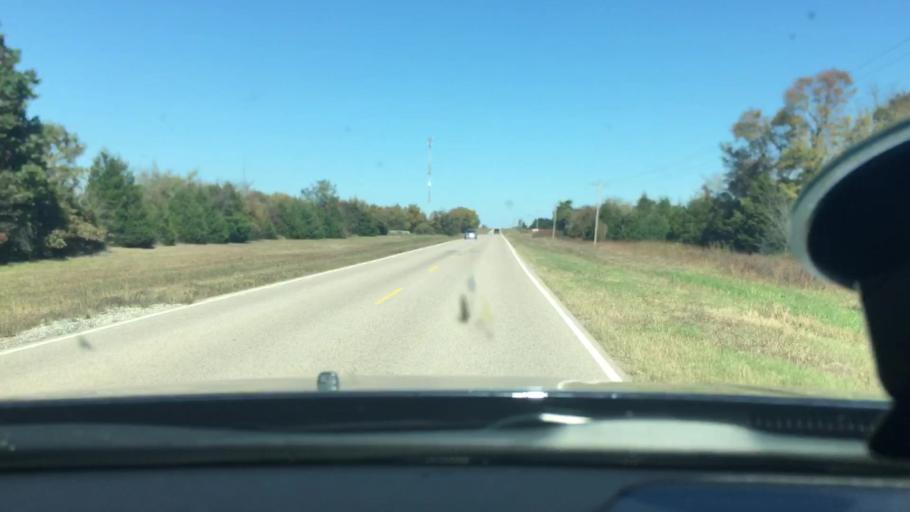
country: US
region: Oklahoma
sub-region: Johnston County
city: Tishomingo
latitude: 34.4239
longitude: -96.6359
